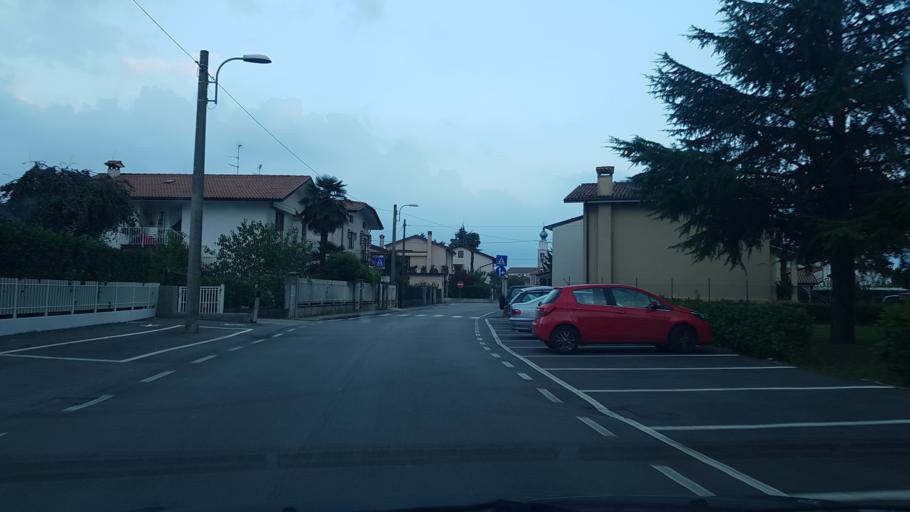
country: IT
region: Friuli Venezia Giulia
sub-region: Provincia di Gorizia
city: Romans d'Isonzo
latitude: 45.8936
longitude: 13.4340
